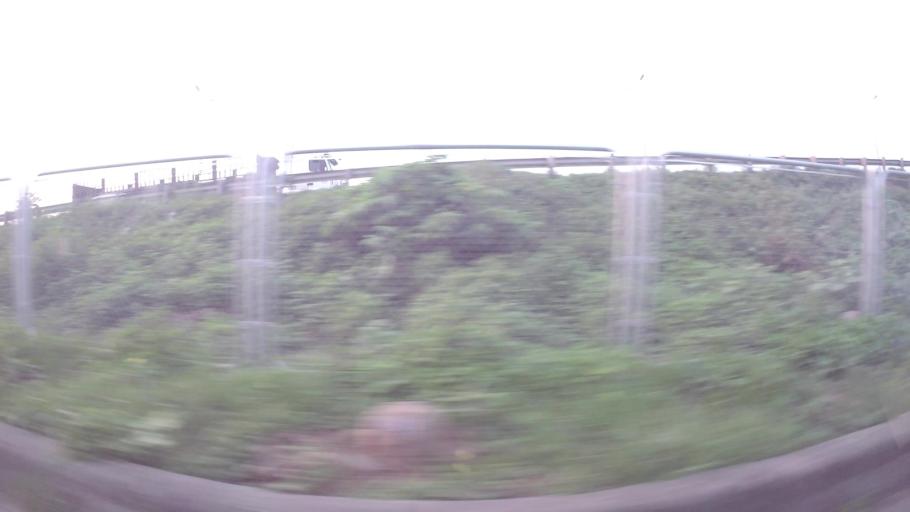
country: VN
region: Ha Noi
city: Van Dien
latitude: 20.9639
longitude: 105.8664
